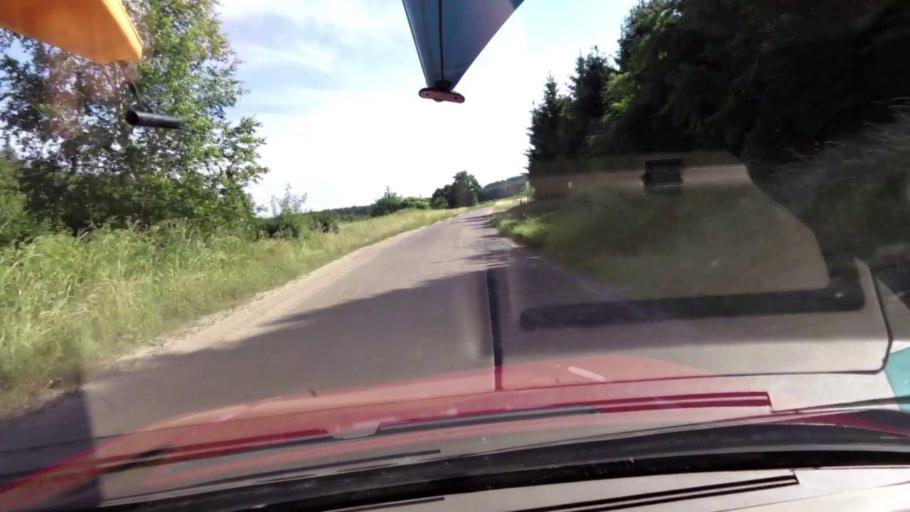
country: PL
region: Pomeranian Voivodeship
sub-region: Powiat slupski
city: Kepice
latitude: 54.1772
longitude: 16.8875
